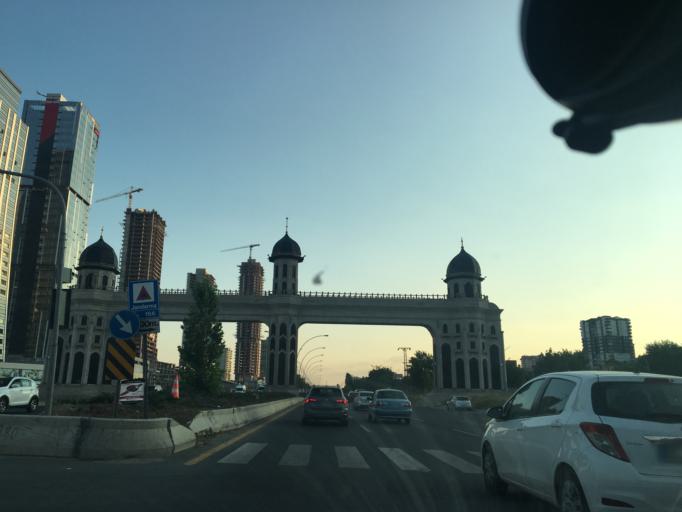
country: TR
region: Ankara
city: Etimesgut
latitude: 39.8809
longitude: 32.6577
